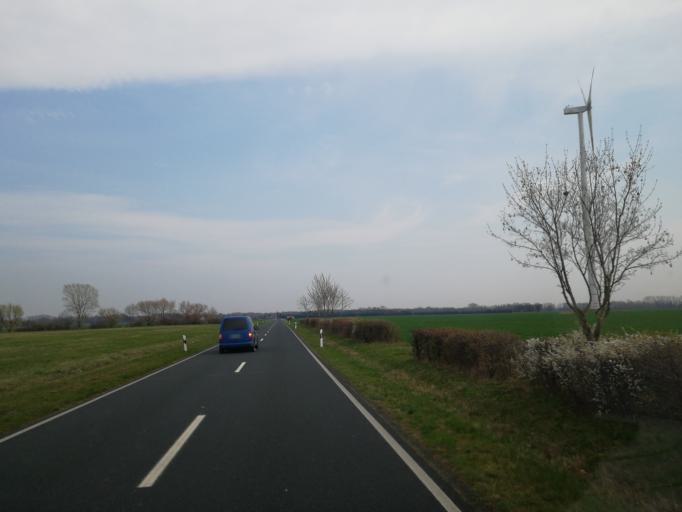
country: DE
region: Brandenburg
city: Elsterwerda
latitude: 51.4481
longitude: 13.4858
